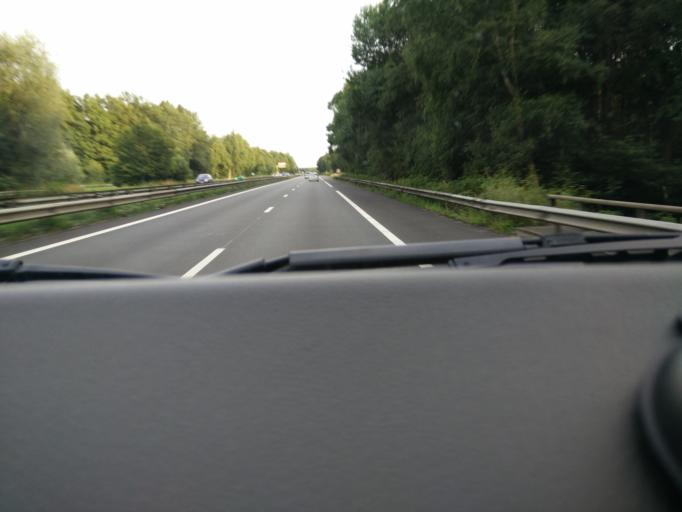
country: FR
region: Nord-Pas-de-Calais
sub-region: Departement du Nord
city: Aubry-du-Hainaut
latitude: 50.3969
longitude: 3.4496
